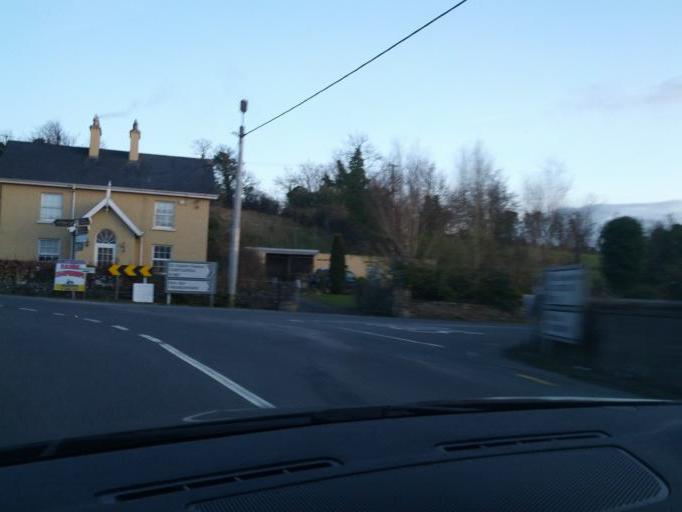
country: IE
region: Connaught
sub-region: Roscommon
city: Boyle
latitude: 53.9627
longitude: -8.2992
